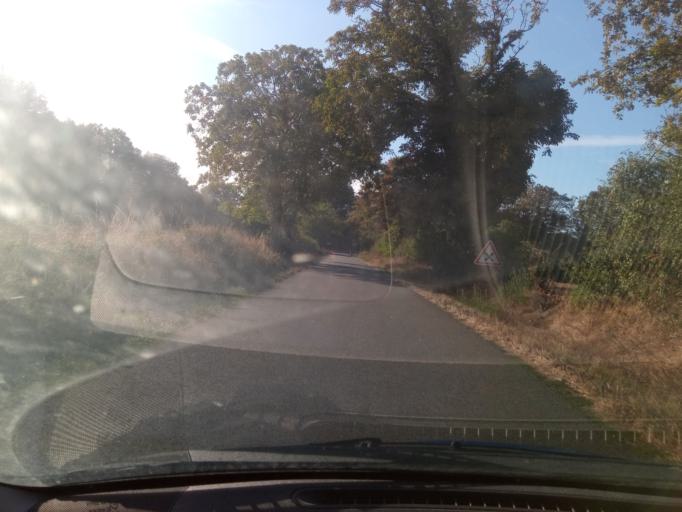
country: FR
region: Poitou-Charentes
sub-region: Departement de la Vienne
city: Montmorillon
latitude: 46.4961
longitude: 0.8318
